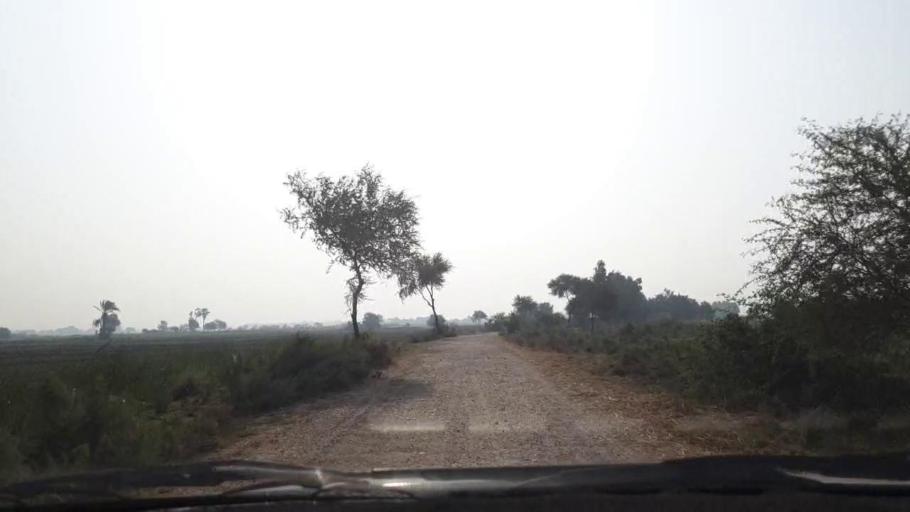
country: PK
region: Sindh
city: Tando Muhammad Khan
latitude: 25.0137
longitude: 68.4523
